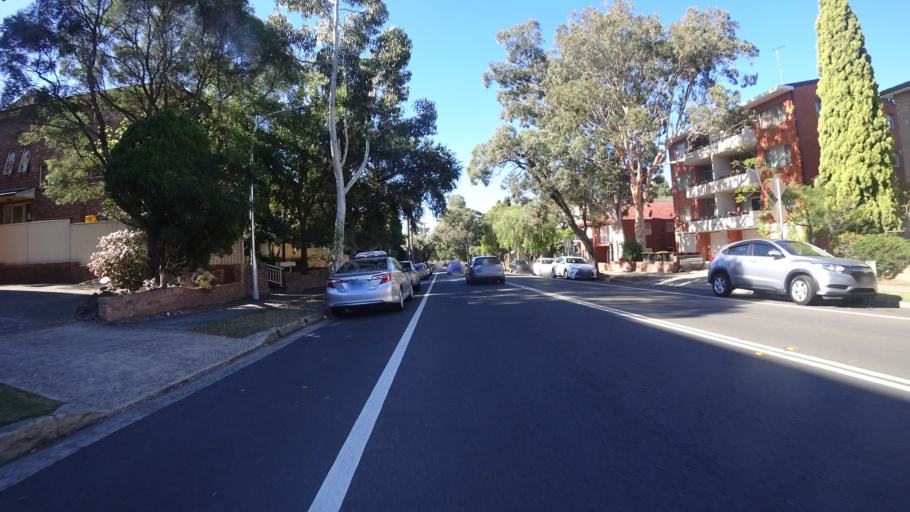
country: AU
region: New South Wales
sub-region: Kogarah
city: Beverly Park
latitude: -33.9606
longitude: 151.1306
